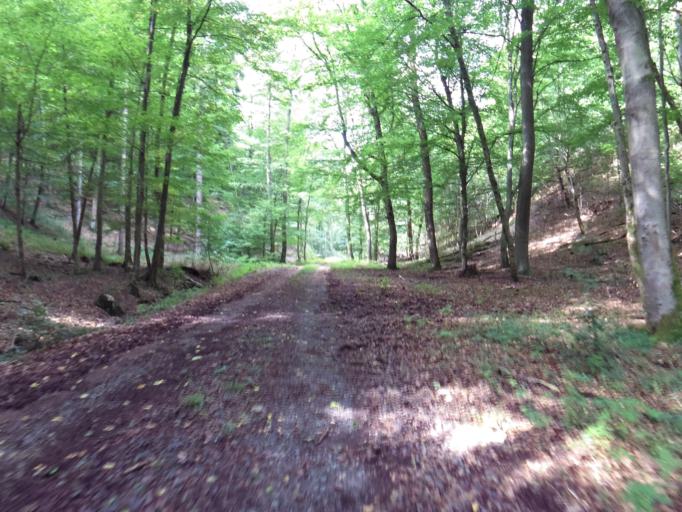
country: DE
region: Rheinland-Pfalz
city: Steinbach am Donnersberg
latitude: 49.5990
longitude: 7.9243
